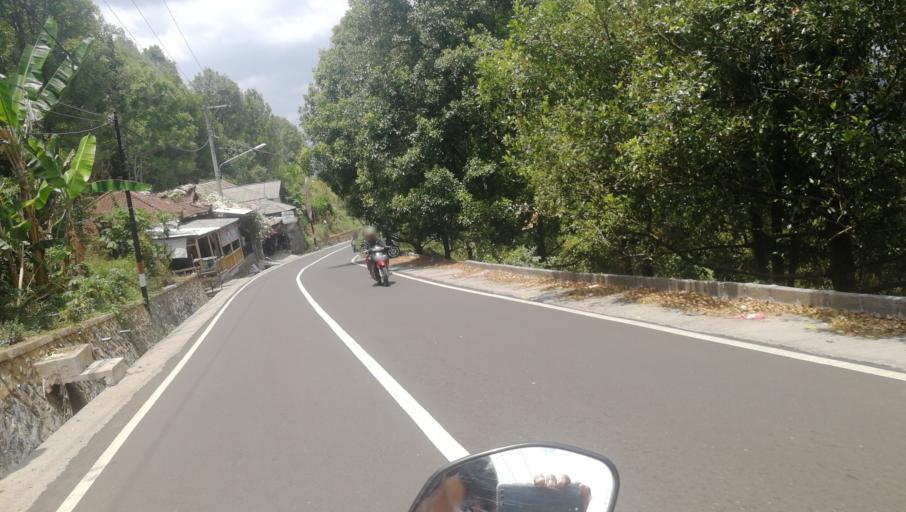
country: ID
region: Bali
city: Banjar Pedawa
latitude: -8.2635
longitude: 115.0438
